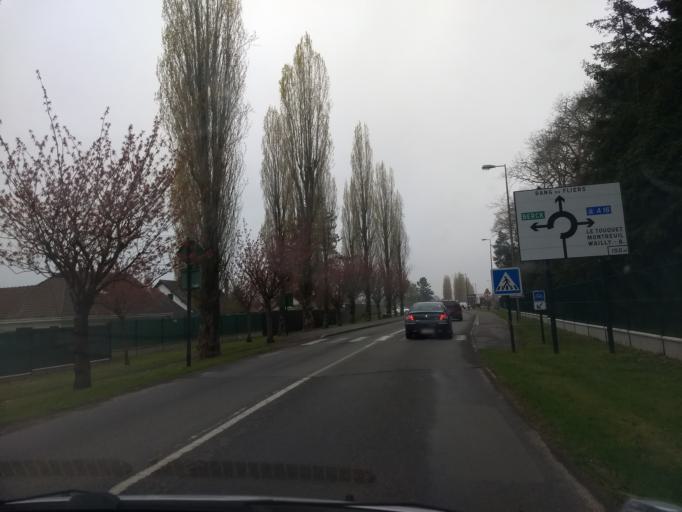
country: FR
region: Nord-Pas-de-Calais
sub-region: Departement du Pas-de-Calais
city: Verton
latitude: 50.4064
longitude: 1.6476
